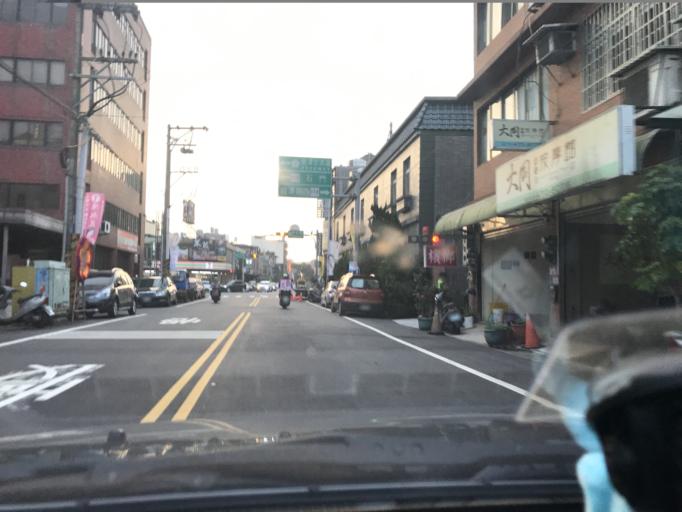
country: TW
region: Taiwan
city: Daxi
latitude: 24.8581
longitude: 121.2198
